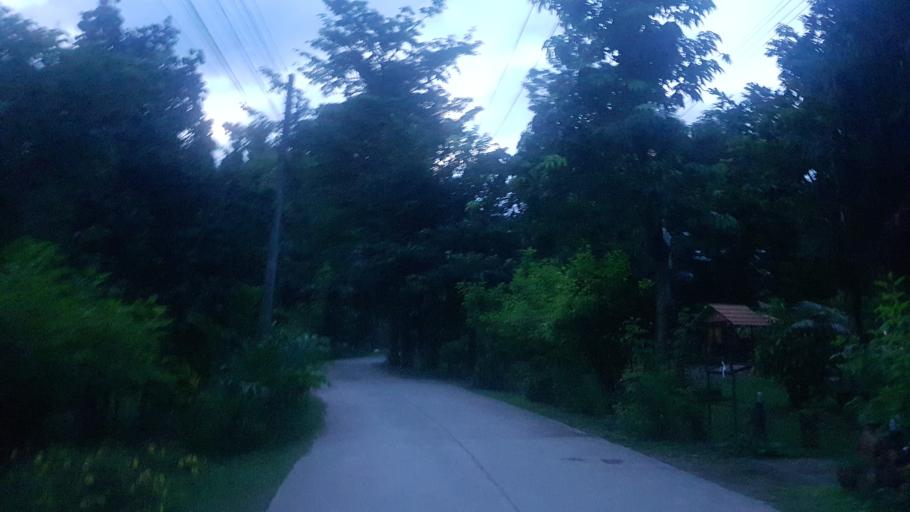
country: TH
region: Phangnga
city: Takua Pa
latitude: 8.9103
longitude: 98.5280
